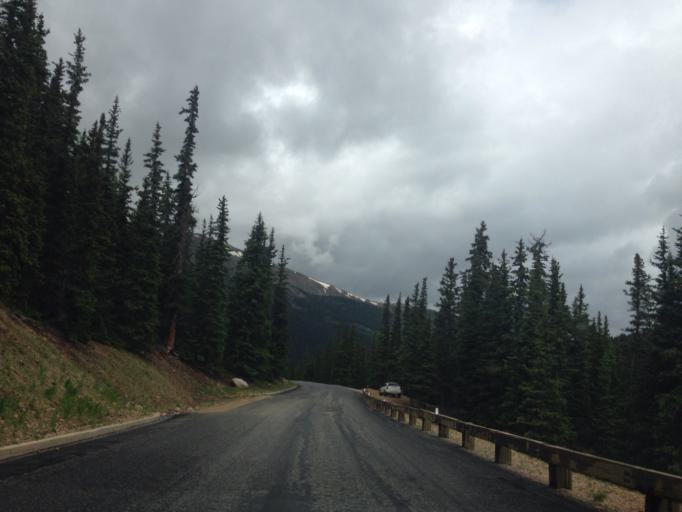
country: US
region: Colorado
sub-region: Clear Creek County
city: Georgetown
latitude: 39.6011
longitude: -105.7094
